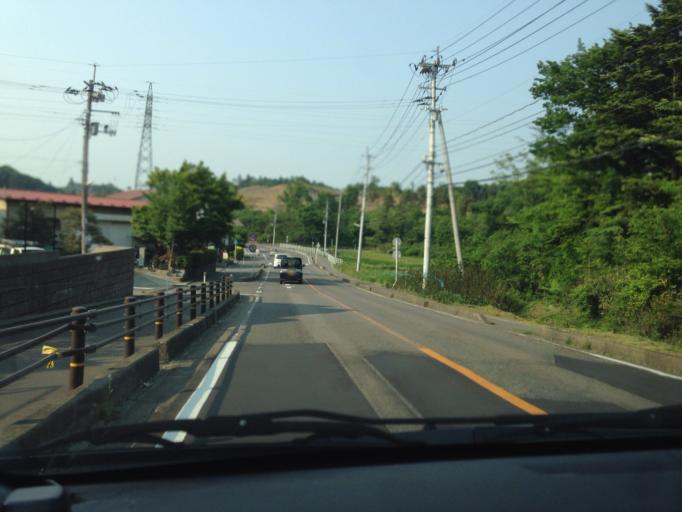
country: JP
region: Tochigi
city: Kuroiso
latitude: 37.1014
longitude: 140.1969
